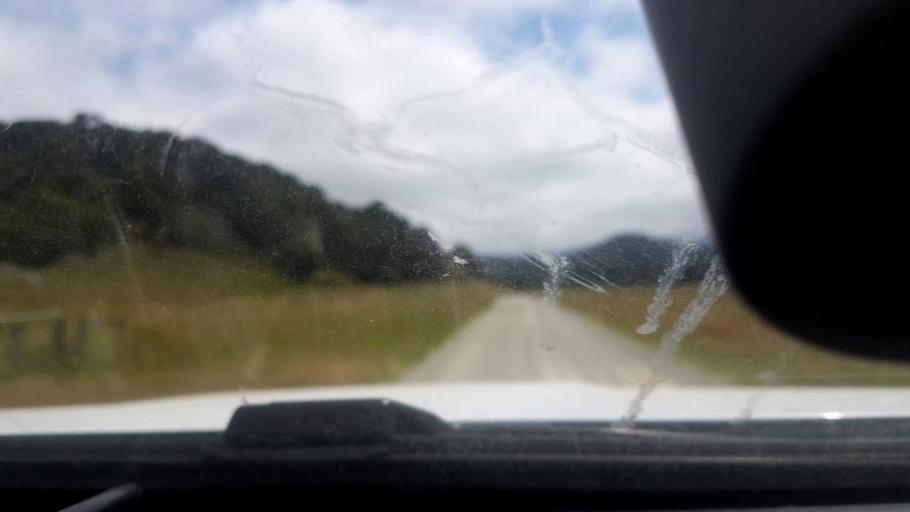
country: NZ
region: Canterbury
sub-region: Timaru District
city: Pleasant Point
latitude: -44.1522
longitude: 171.0908
